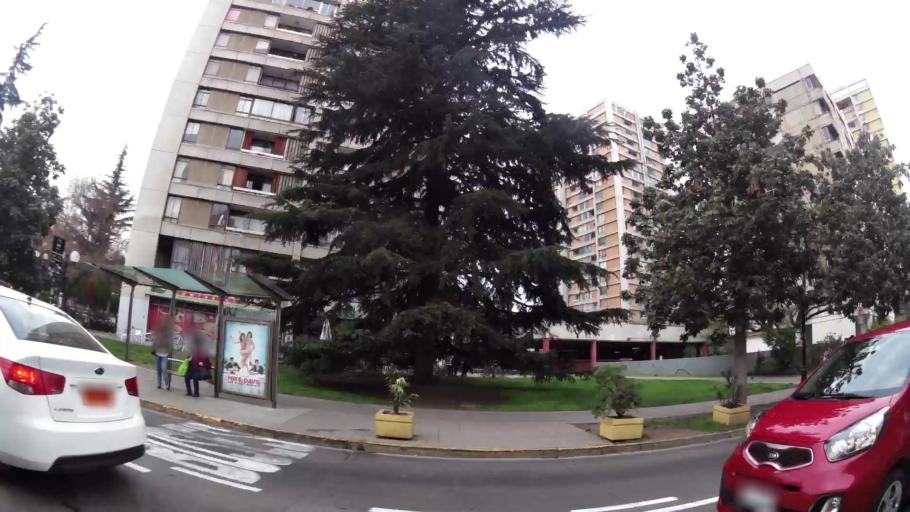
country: CL
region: Santiago Metropolitan
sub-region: Provincia de Santiago
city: Santiago
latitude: -33.4398
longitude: -70.6135
